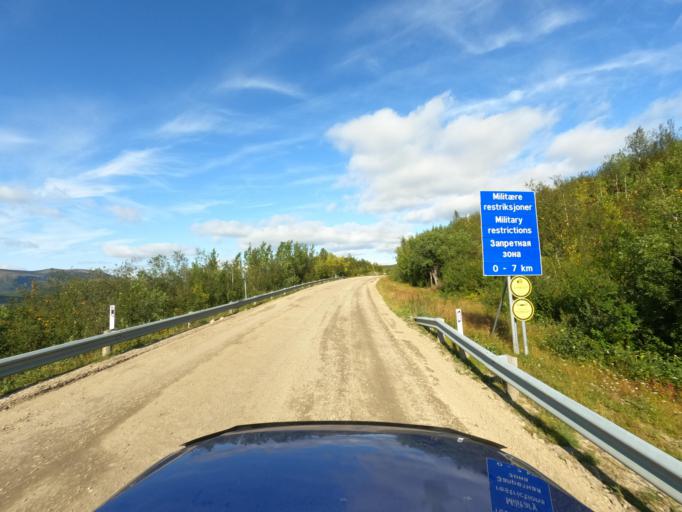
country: NO
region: Finnmark Fylke
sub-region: Porsanger
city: Lakselv
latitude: 69.8810
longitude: 25.0219
